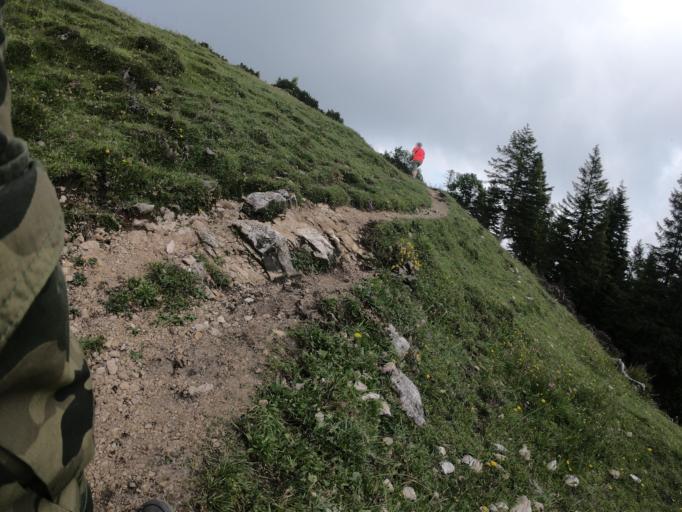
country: DE
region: Bavaria
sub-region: Upper Bavaria
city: Aschau im Chiemgau
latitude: 47.7628
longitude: 12.3681
